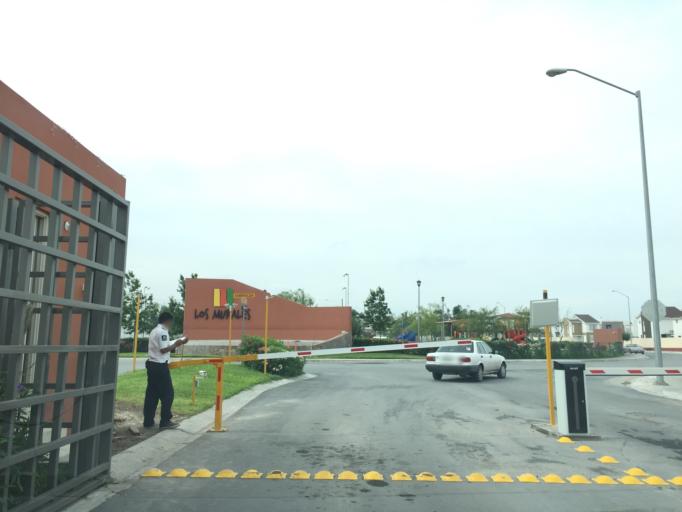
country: MX
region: Nuevo Leon
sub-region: Apodaca
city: Fraccionamiento Cosmopolis Octavo Sector
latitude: 25.8013
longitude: -100.2214
